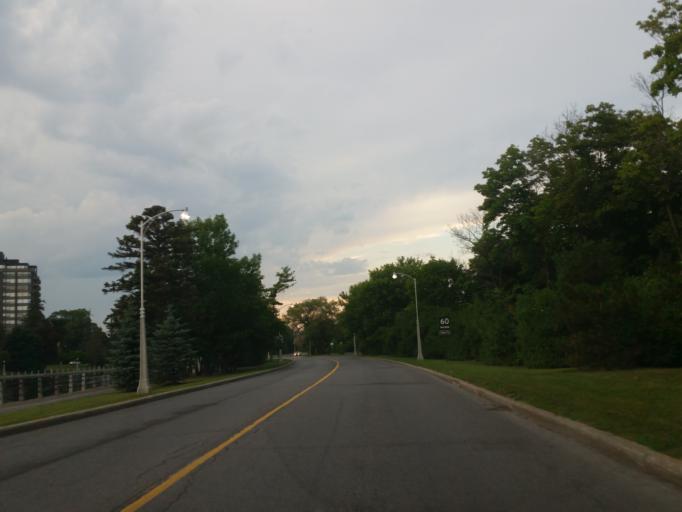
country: CA
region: Ontario
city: Ottawa
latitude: 45.4049
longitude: -75.6803
